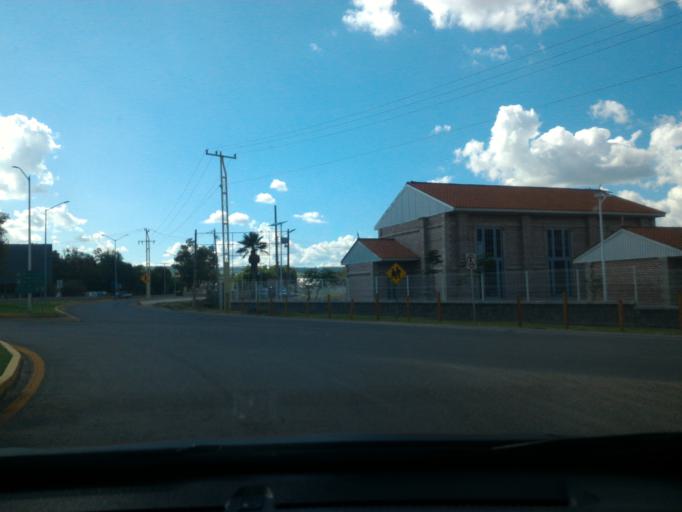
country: MX
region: Guanajuato
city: Ciudad Manuel Doblado
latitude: 20.7253
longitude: -101.9425
